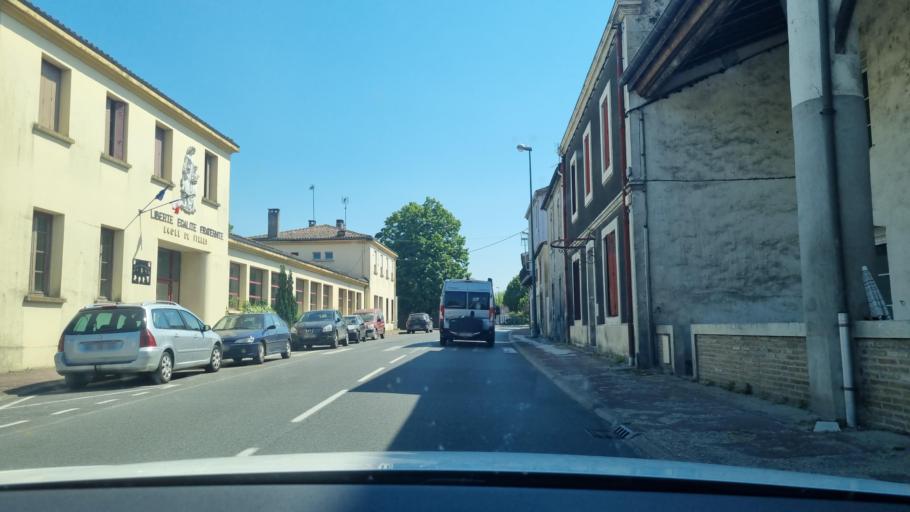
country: FR
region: Aquitaine
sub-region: Departement de la Gironde
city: Prechac
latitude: 44.2896
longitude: -0.2626
